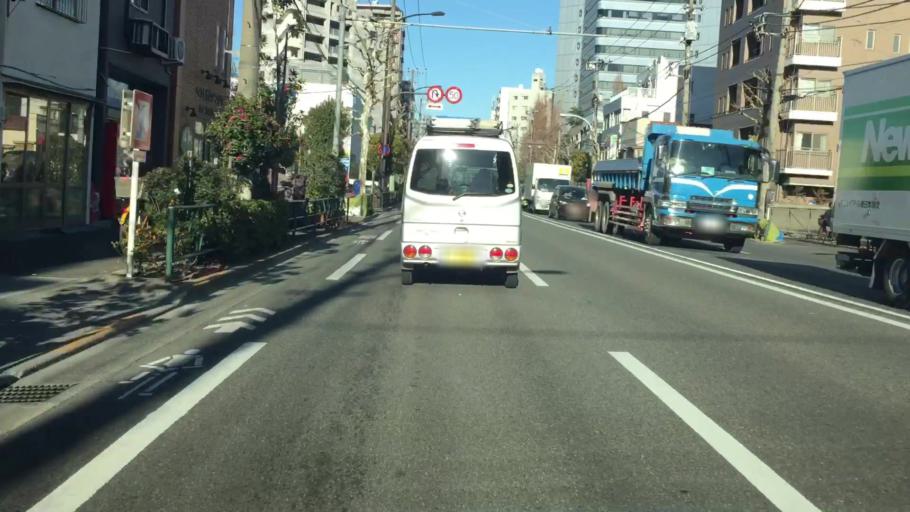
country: JP
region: Saitama
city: Kawaguchi
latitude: 35.7523
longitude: 139.7463
